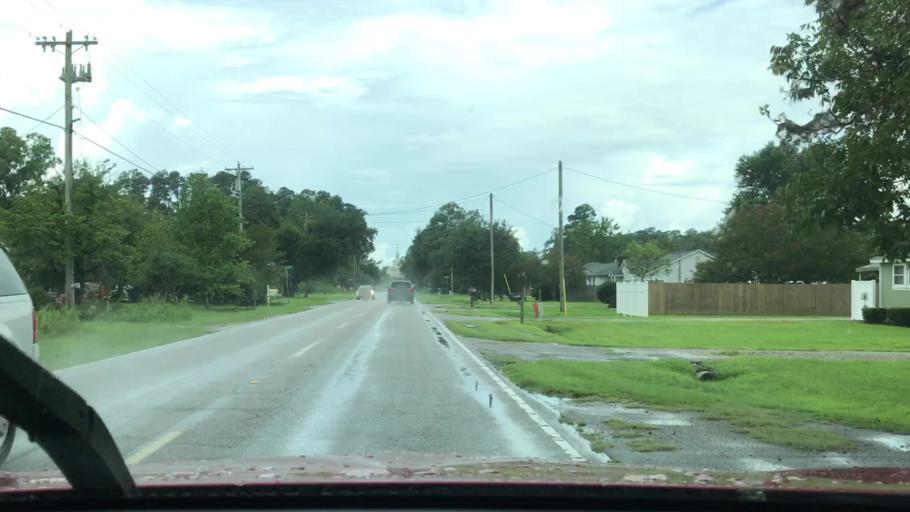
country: US
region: South Carolina
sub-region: Horry County
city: Red Hill
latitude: 33.8500
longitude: -79.0187
